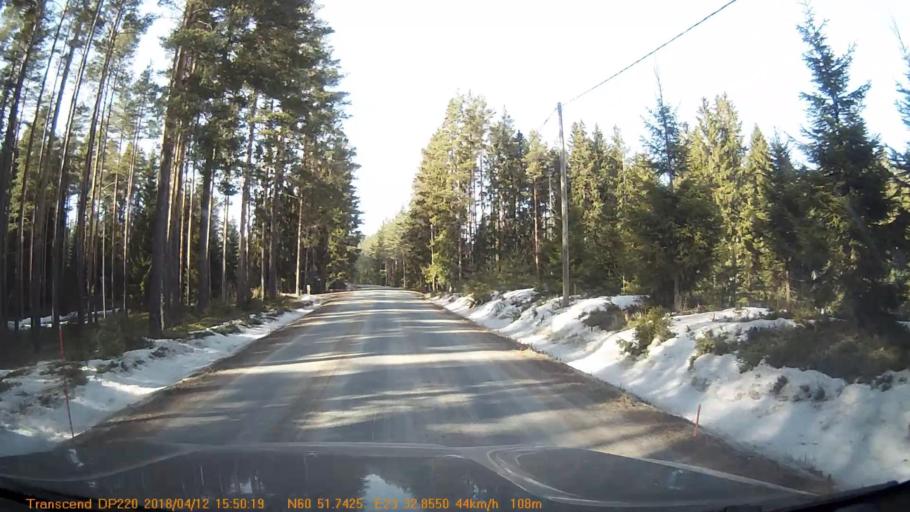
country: FI
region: Haeme
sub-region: Forssa
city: Forssa
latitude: 60.8626
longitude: 23.5475
